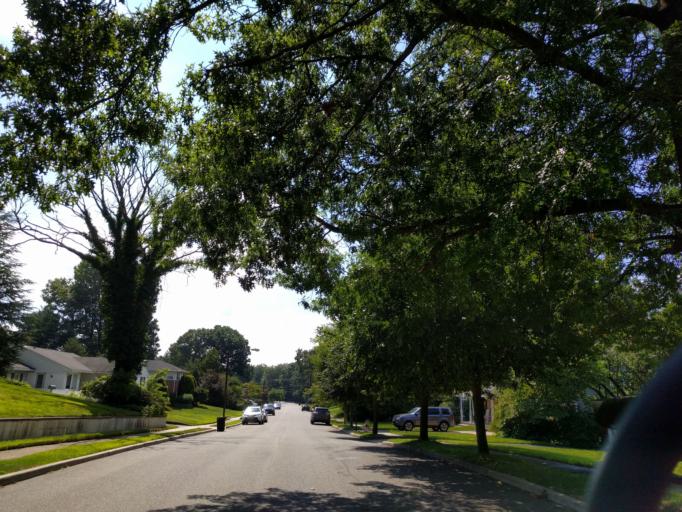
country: US
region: New York
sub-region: Nassau County
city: East Norwich
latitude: 40.8547
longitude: -73.5289
